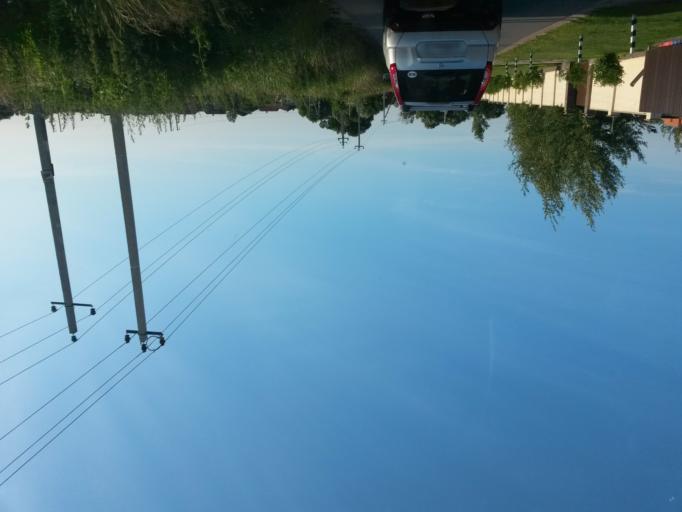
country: RU
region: Moskovskaya
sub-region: Podol'skiy Rayon
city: Podol'sk
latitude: 55.3962
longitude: 37.6209
